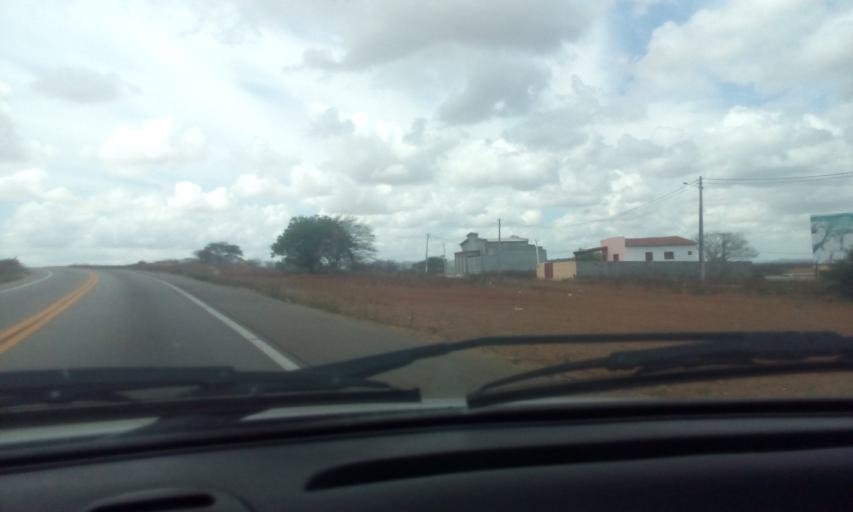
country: BR
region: Rio Grande do Norte
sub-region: Tangara
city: Tangara
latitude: -6.1136
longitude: -35.7162
